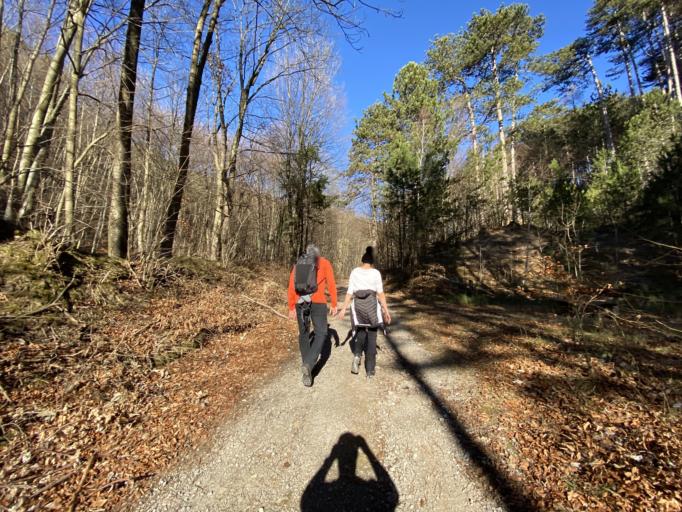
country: AT
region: Lower Austria
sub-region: Politischer Bezirk Baden
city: Berndorf
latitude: 47.9818
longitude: 16.1422
